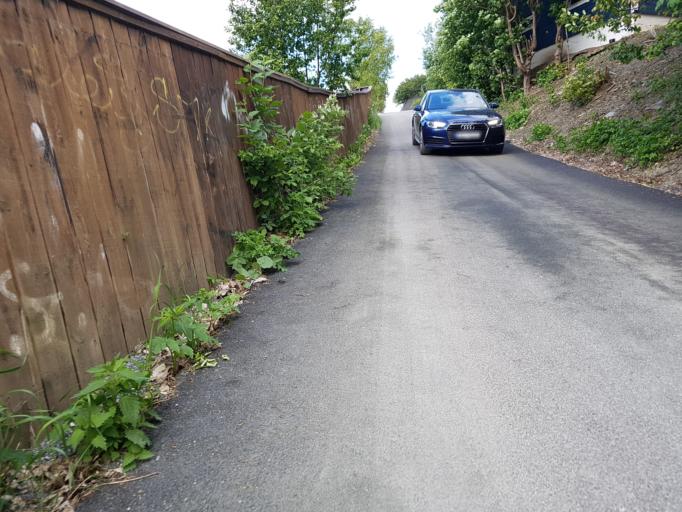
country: NO
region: Sor-Trondelag
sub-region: Trondheim
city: Trondheim
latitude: 63.4345
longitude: 10.4347
